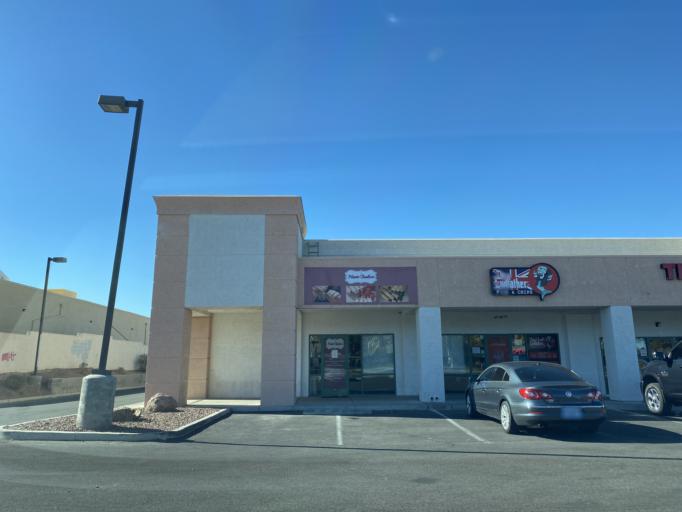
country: US
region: Nevada
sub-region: Clark County
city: Whitney
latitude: 36.0738
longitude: -115.0826
